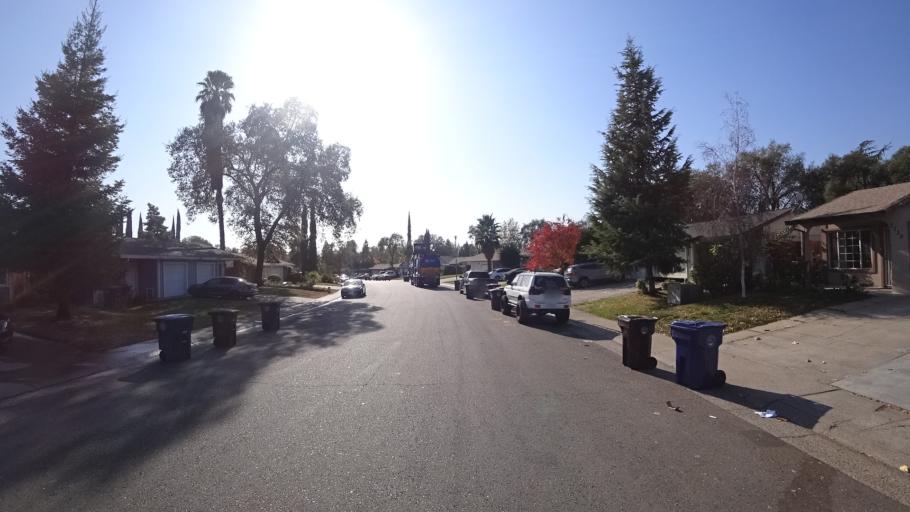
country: US
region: California
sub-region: Sacramento County
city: Citrus Heights
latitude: 38.6838
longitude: -121.2785
